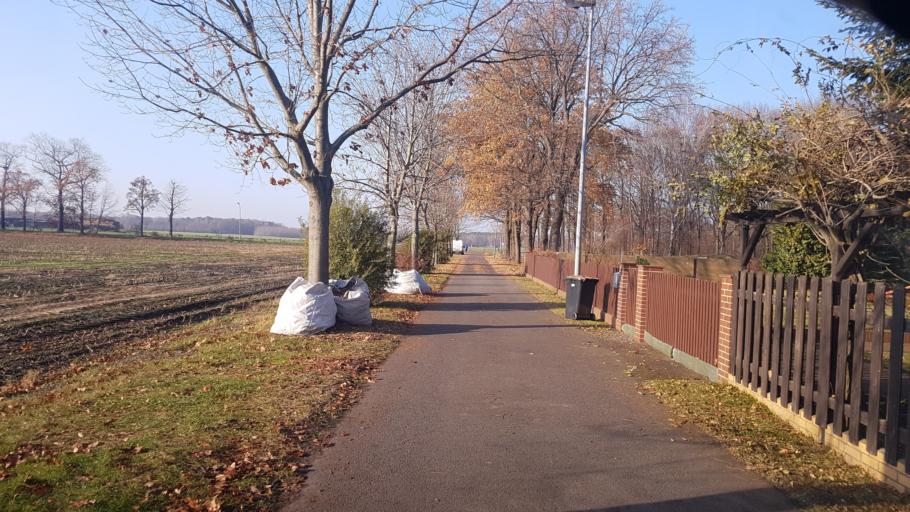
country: DE
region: Brandenburg
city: Tettau
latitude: 51.4363
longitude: 13.7332
